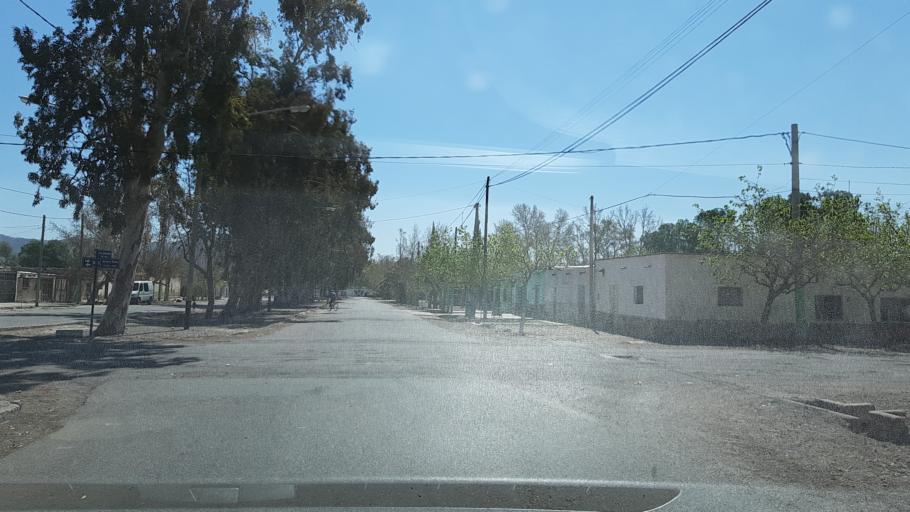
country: AR
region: San Juan
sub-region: Departamento de Rivadavia
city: Rivadavia
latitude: -31.5257
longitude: -68.6327
